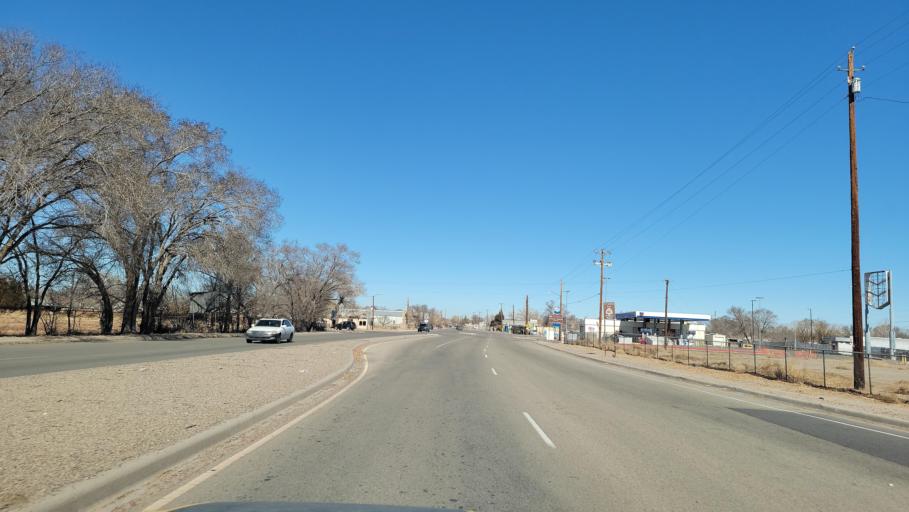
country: US
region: New Mexico
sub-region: Bernalillo County
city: South Valley
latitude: 34.9494
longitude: -106.6940
